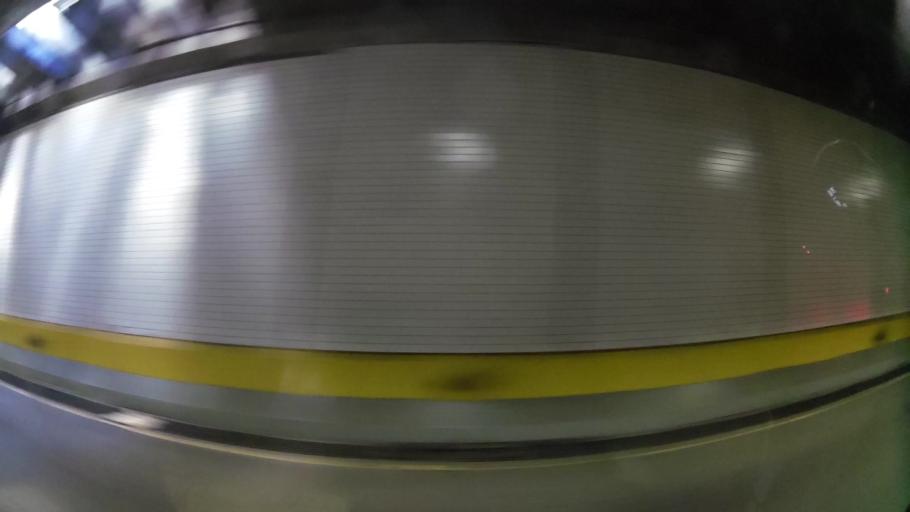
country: DO
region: Santo Domingo
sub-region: Santo Domingo
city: Santo Domingo Este
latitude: 18.4852
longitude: -69.8682
